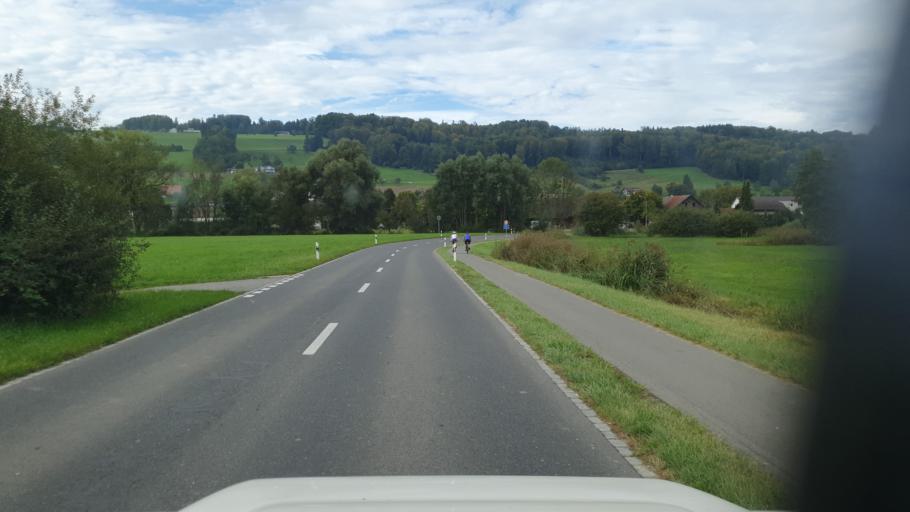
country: CH
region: Lucerne
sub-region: Hochdorf District
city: Hitzkirch
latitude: 47.2444
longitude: 8.2321
